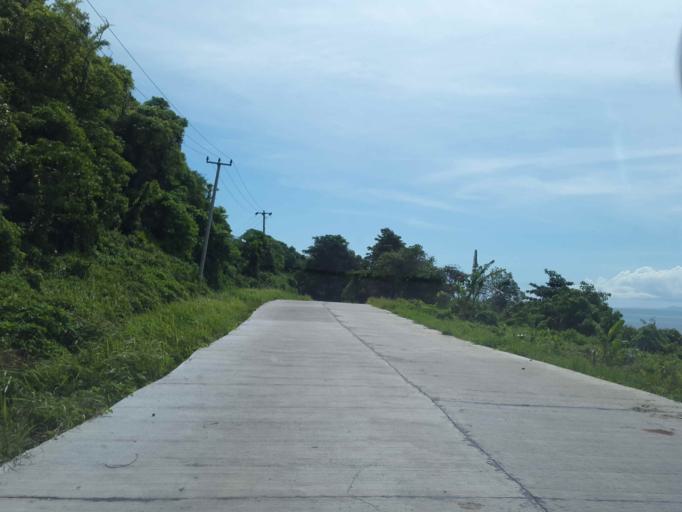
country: ID
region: Banten
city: Citeureup
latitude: -6.5051
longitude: 105.6403
